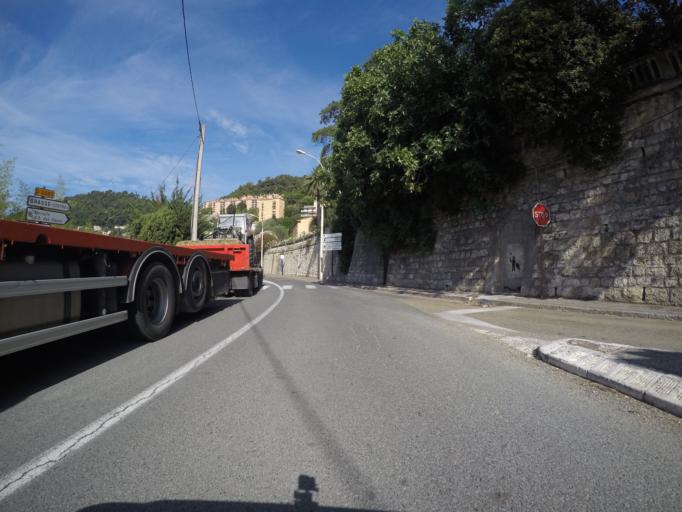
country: FR
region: Provence-Alpes-Cote d'Azur
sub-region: Departement des Alpes-Maritimes
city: Grasse
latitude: 43.6637
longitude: 6.9274
